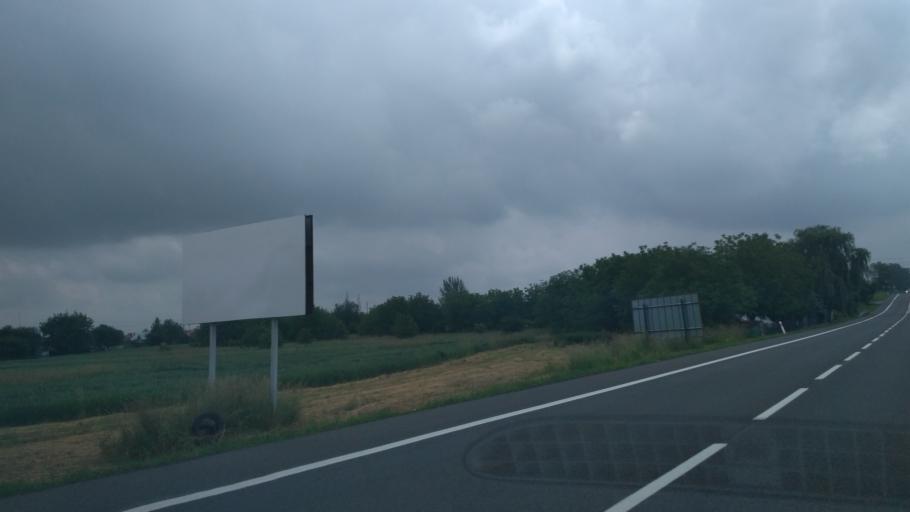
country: PL
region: Subcarpathian Voivodeship
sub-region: Powiat przeworski
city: Przeworsk
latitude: 50.0563
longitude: 22.5058
